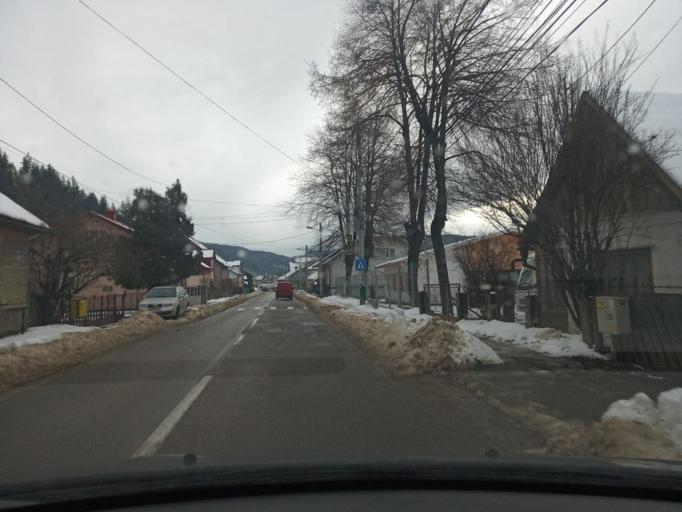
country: RO
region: Suceava
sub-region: Oras Gura Humorului
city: Gura Humorului
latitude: 47.5646
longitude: 25.8846
